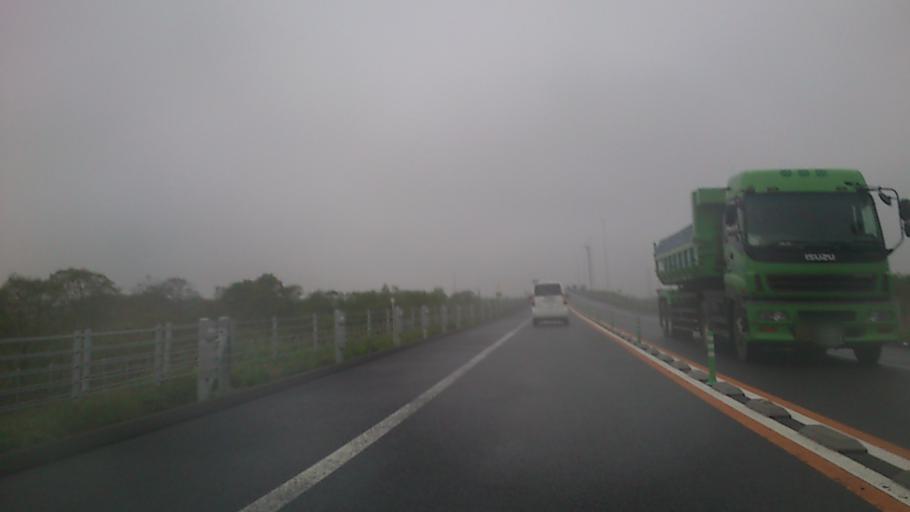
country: JP
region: Hokkaido
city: Kushiro
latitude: 43.0328
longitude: 144.3920
